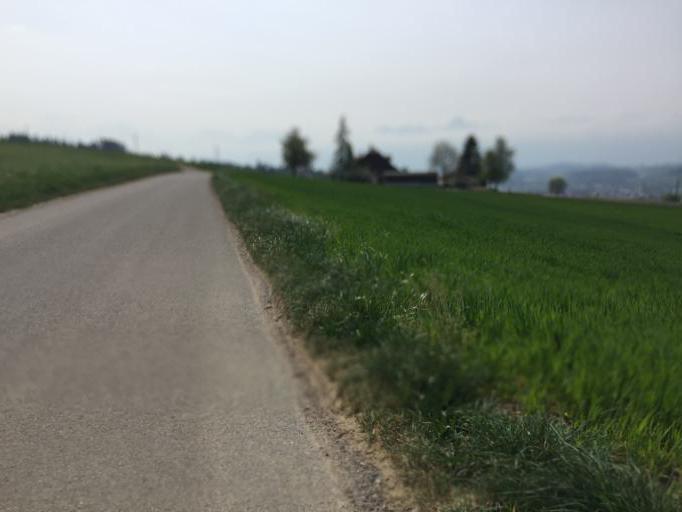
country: CH
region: Bern
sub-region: Bern-Mittelland District
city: Taegertschi
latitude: 46.8637
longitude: 7.5817
